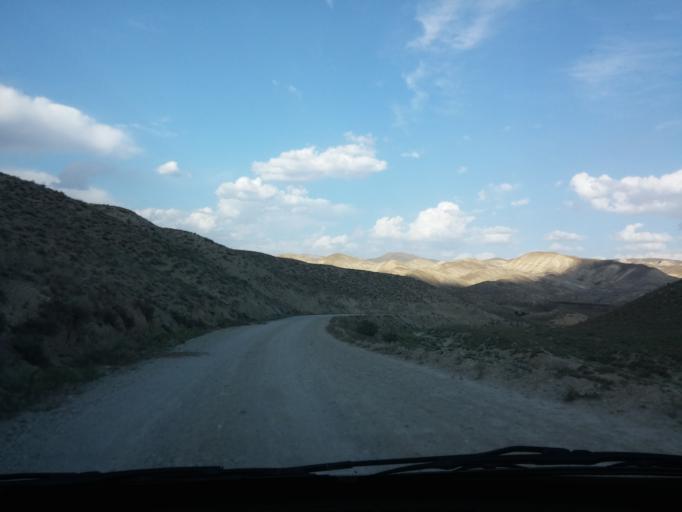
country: IR
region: Tehran
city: Damavand
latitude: 35.5332
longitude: 52.2311
